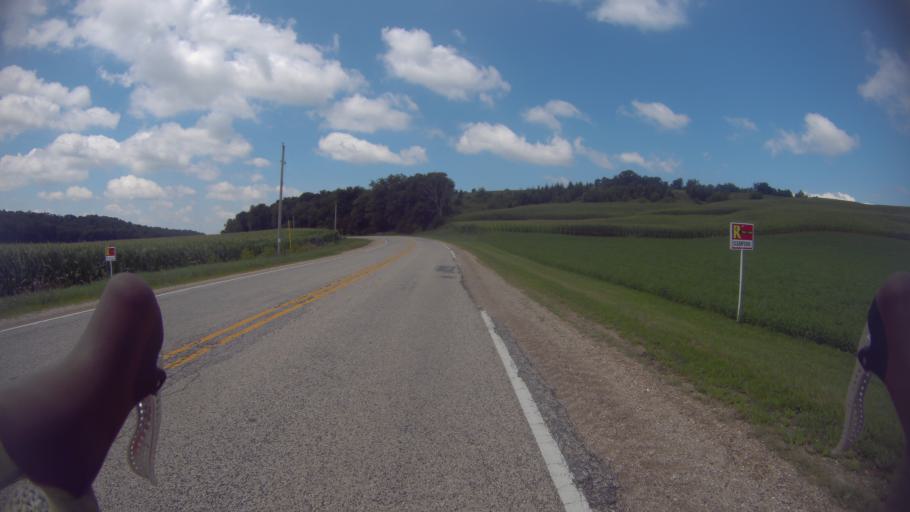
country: US
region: Wisconsin
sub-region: Columbia County
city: Lodi
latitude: 43.2493
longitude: -89.6145
